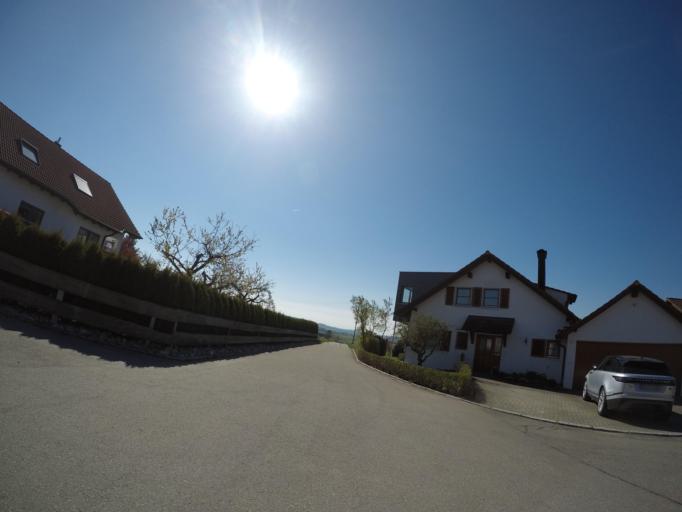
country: DE
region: Baden-Wuerttemberg
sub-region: Tuebingen Region
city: Wilhelmsdorf
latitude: 47.8623
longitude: 9.4300
